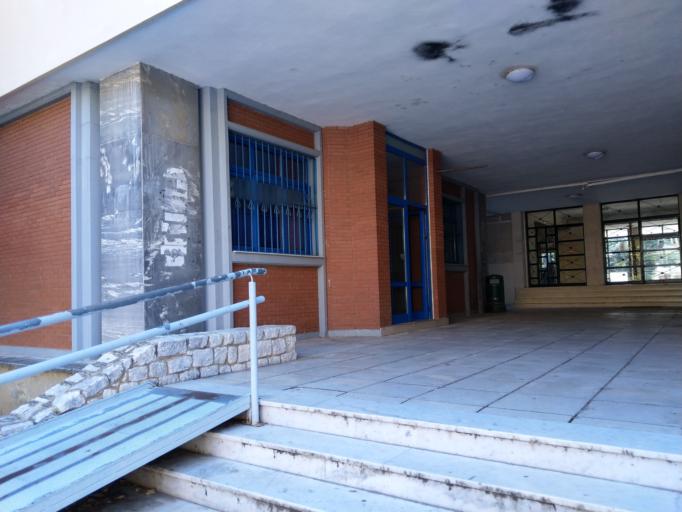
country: GR
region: East Macedonia and Thrace
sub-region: Nomos Rodopis
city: Komotini
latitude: 41.1184
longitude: 25.4065
